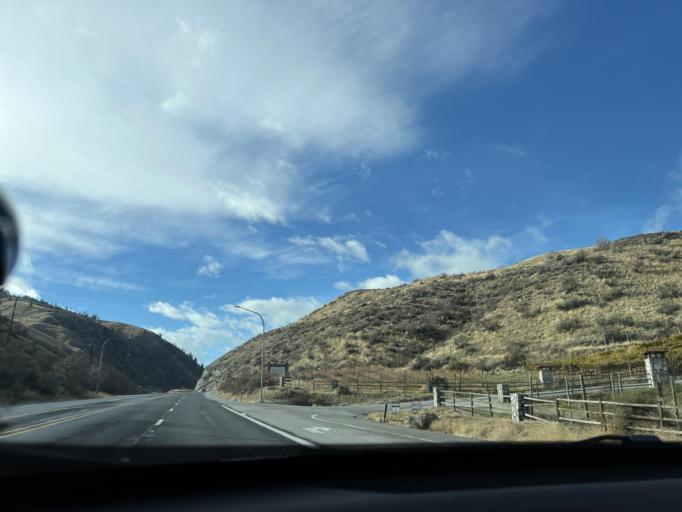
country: US
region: Washington
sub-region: Chelan County
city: Manson
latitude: 47.8369
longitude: -120.1080
